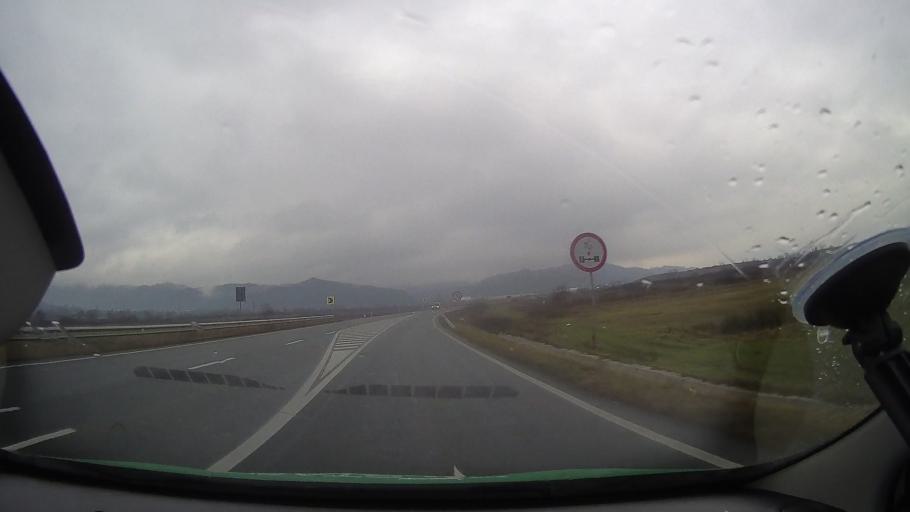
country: RO
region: Hunedoara
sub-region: Comuna Baia de Cris
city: Baia de Cris
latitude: 46.1677
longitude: 22.7434
